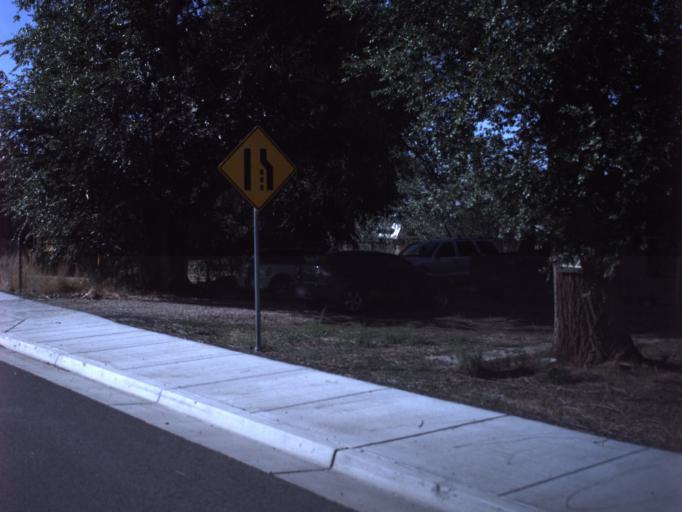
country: US
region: Utah
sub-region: Juab County
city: Nephi
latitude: 39.5543
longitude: -111.8639
